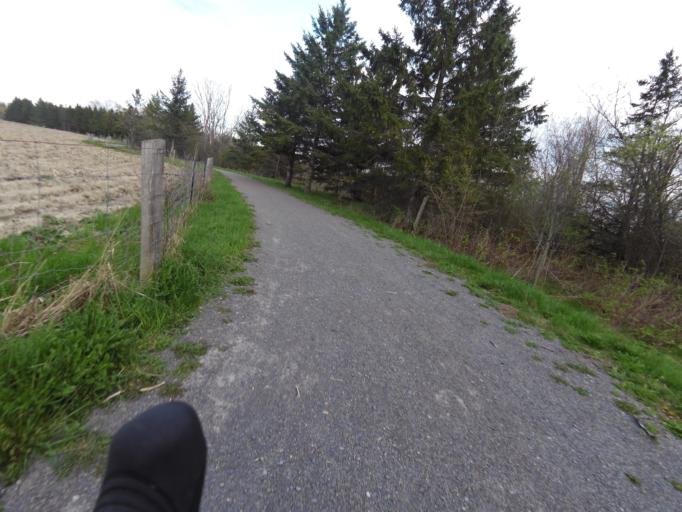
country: CA
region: Ontario
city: Ottawa
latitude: 45.3203
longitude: -75.7041
